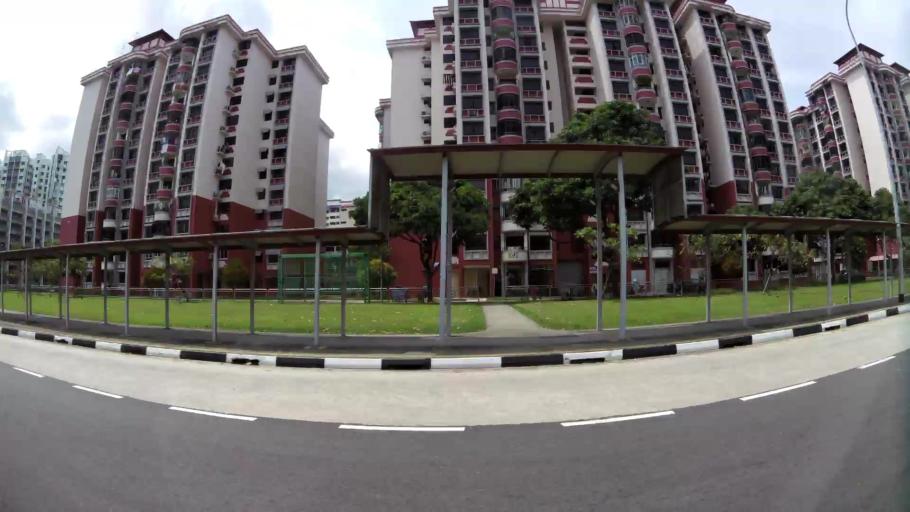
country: MY
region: Johor
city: Johor Bahru
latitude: 1.3429
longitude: 103.7078
